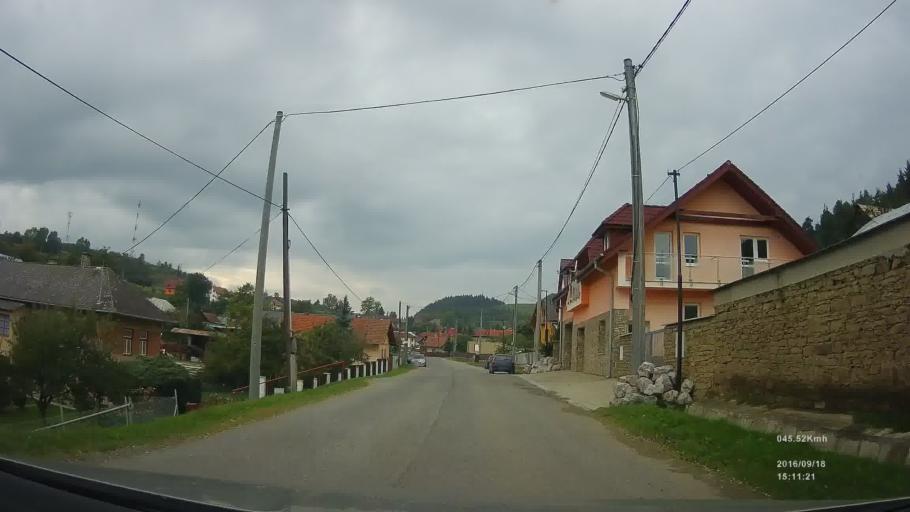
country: SK
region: Presovsky
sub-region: Okres Presov
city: Levoca
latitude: 49.0192
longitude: 20.4912
